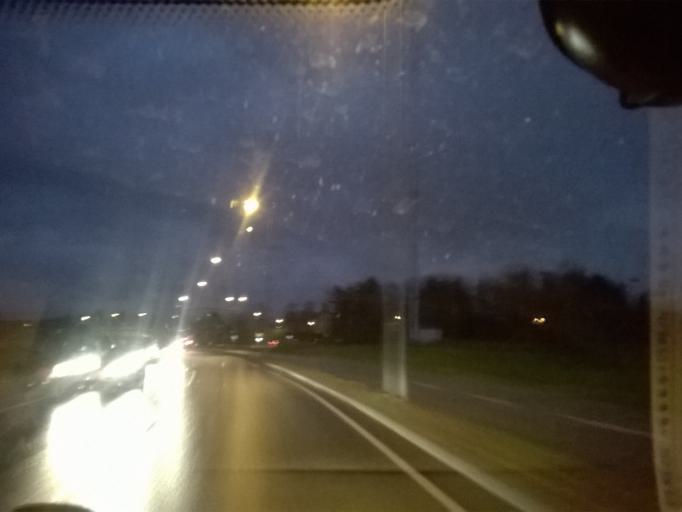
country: EE
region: Harju
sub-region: Viimsi vald
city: Viimsi
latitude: 59.4940
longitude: 24.8768
